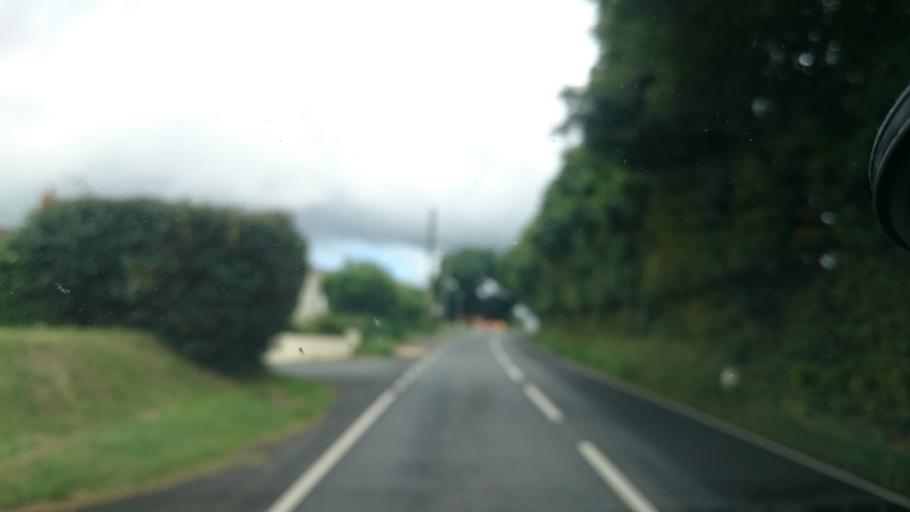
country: GB
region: Wales
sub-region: Pembrokeshire
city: Llangwm
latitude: 51.7338
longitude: -4.9213
